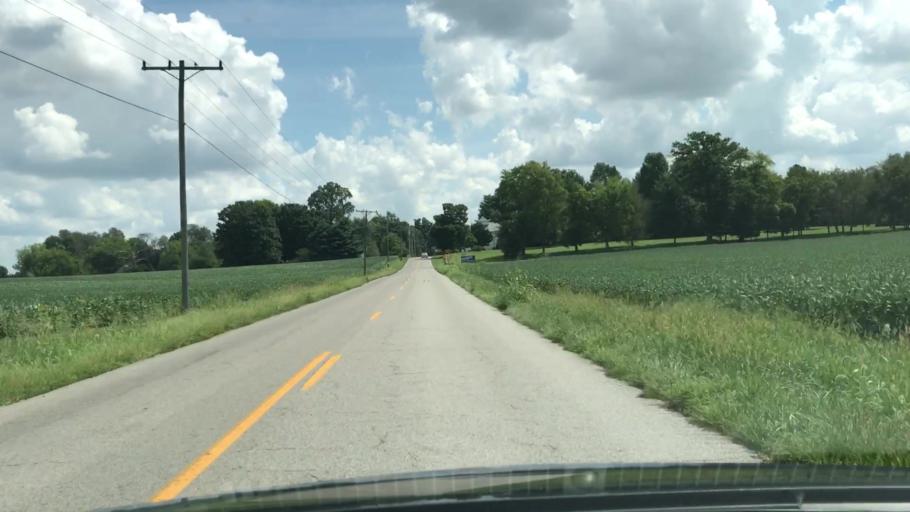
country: US
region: Kentucky
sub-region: Todd County
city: Guthrie
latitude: 36.7183
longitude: -87.0742
